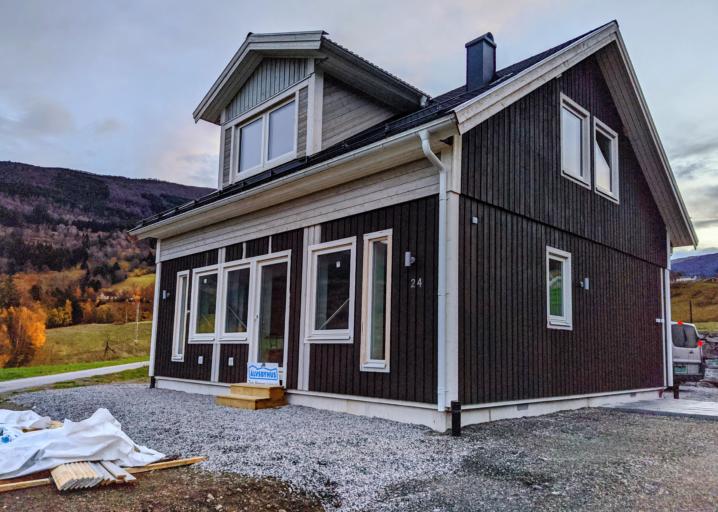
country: NO
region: Sogn og Fjordane
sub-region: Vik
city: Vikoyri
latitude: 61.0738
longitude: 6.5622
